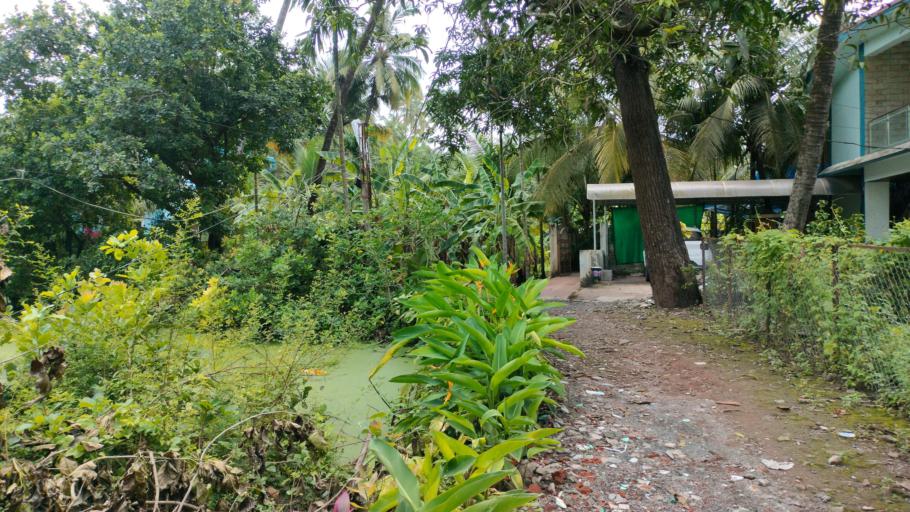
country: IN
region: Maharashtra
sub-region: Thane
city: Bhayandar
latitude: 19.3568
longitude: 72.8024
